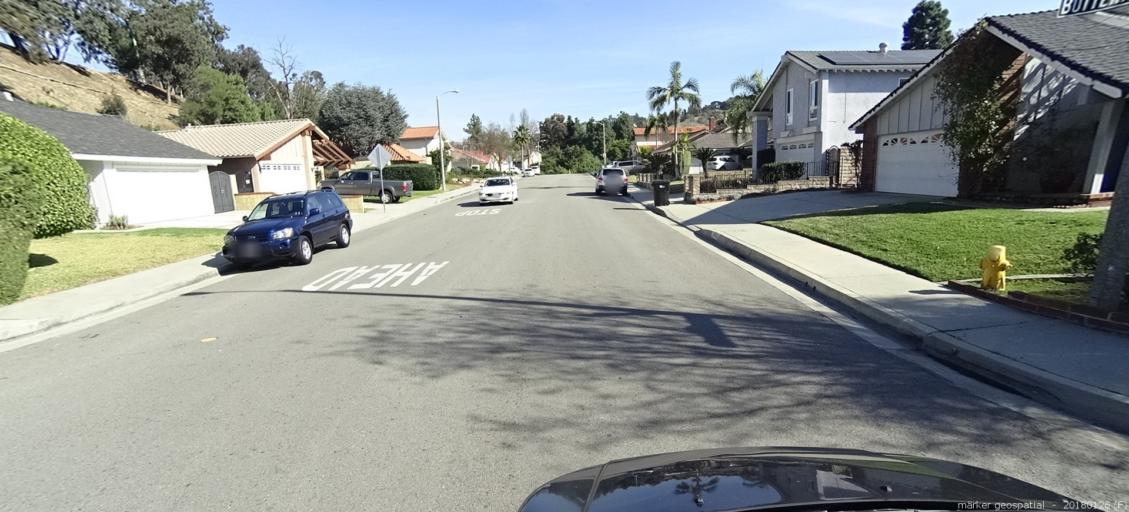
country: US
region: California
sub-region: Los Angeles County
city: Diamond Bar
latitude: 33.9932
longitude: -117.8197
